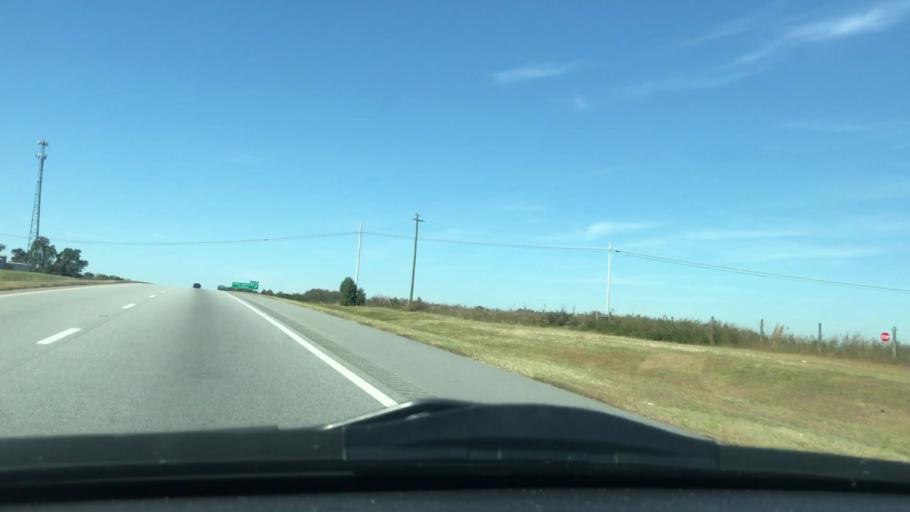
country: US
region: North Carolina
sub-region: Randolph County
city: Archdale
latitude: 35.8686
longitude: -79.8949
